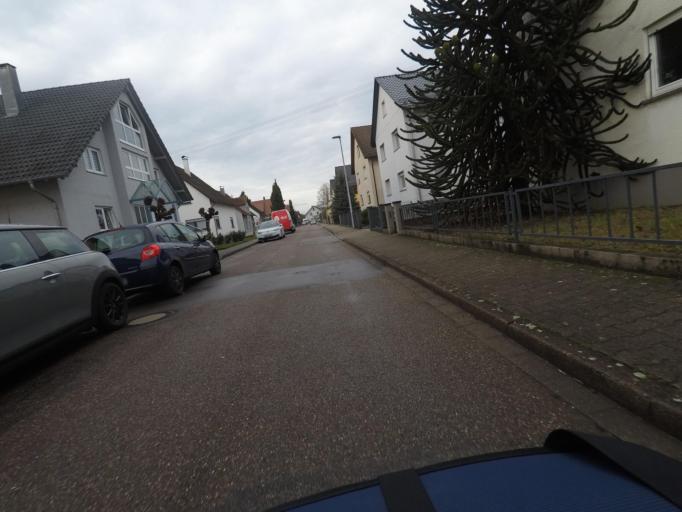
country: DE
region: Baden-Wuerttemberg
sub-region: Karlsruhe Region
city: Rheinau
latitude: 48.8604
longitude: 8.1597
